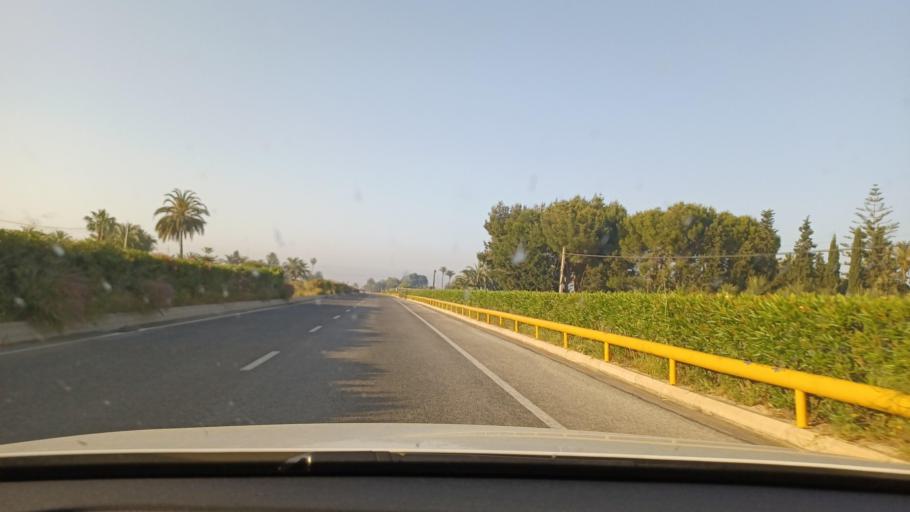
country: ES
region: Valencia
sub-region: Provincia de Alicante
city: Elche
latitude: 38.2033
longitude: -0.7002
